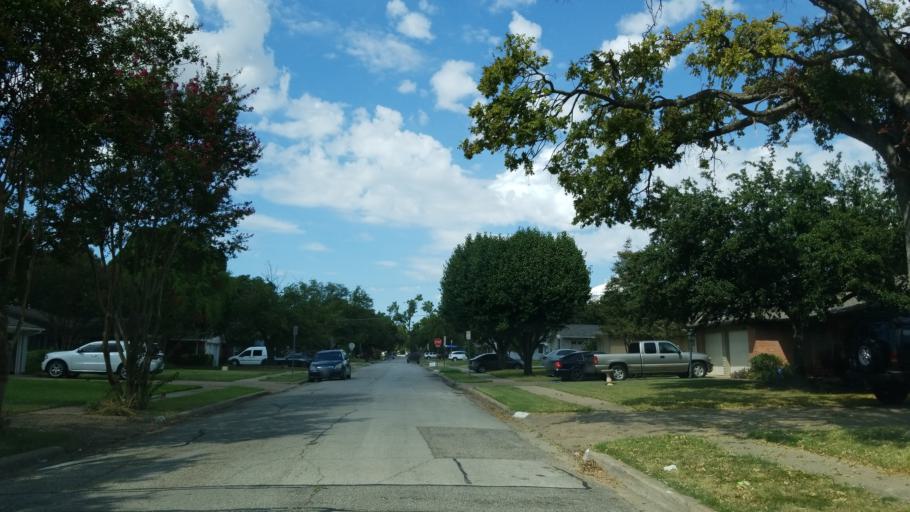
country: US
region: Texas
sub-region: Dallas County
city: Richardson
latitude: 32.9531
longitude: -96.7651
